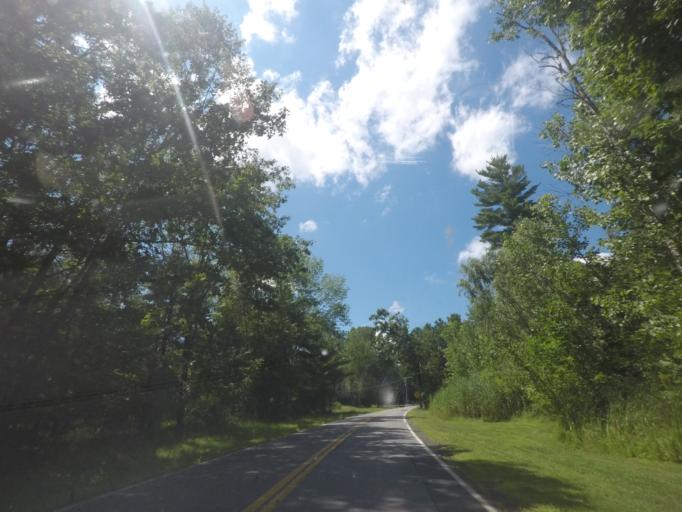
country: US
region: New York
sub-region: Albany County
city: Westmere
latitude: 42.6911
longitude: -73.9096
